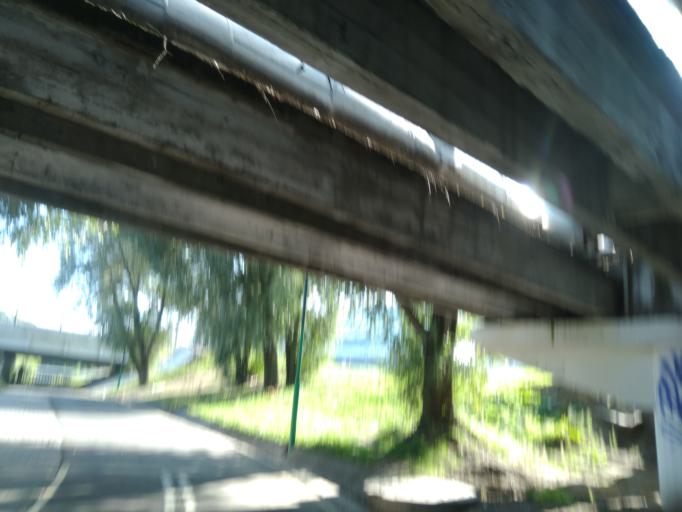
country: BY
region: Minsk
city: Minsk
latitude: 53.8872
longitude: 27.5712
